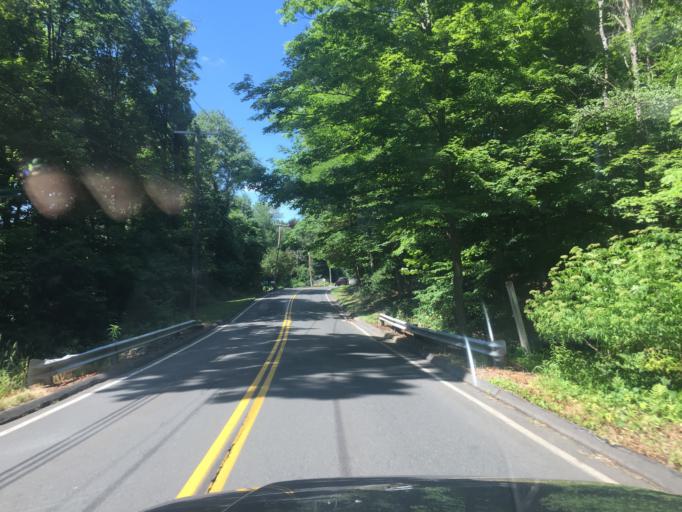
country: US
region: Connecticut
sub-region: Hartford County
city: Farmington
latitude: 41.7498
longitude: -72.8152
